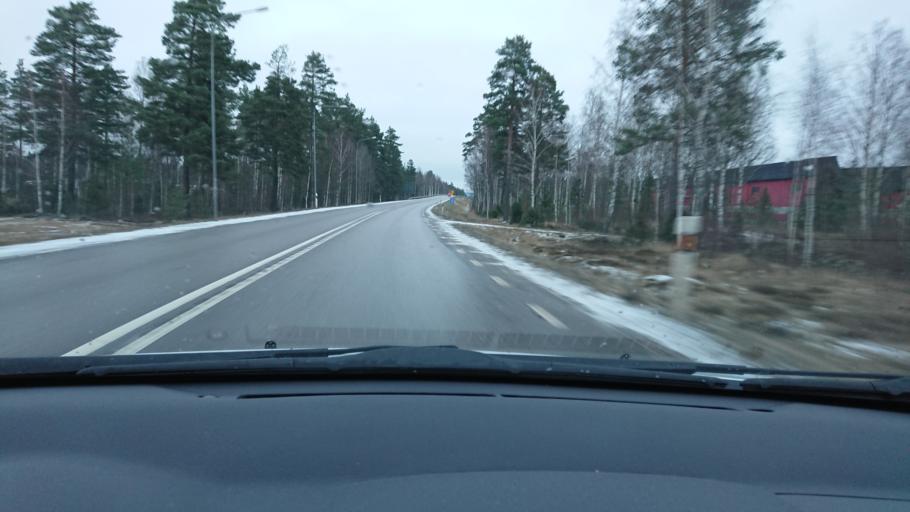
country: SE
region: Kalmar
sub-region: Hultsfreds Kommun
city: Hultsfred
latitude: 57.5017
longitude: 15.8230
